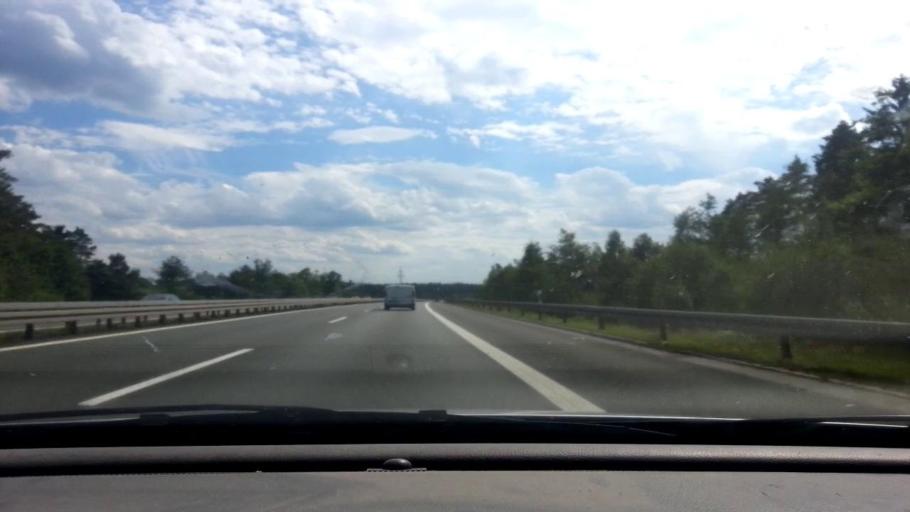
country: DE
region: Bavaria
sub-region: Upper Palatinate
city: Wiesau
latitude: 49.8933
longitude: 12.2183
